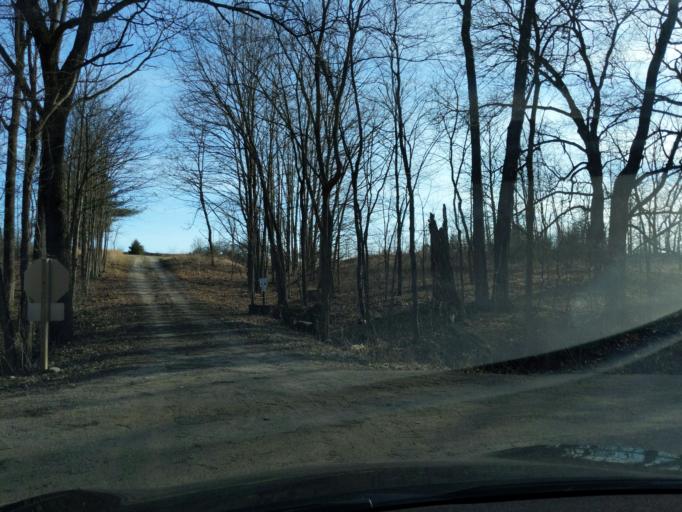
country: US
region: Michigan
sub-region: Ionia County
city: Ionia
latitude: 42.9576
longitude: -85.1311
